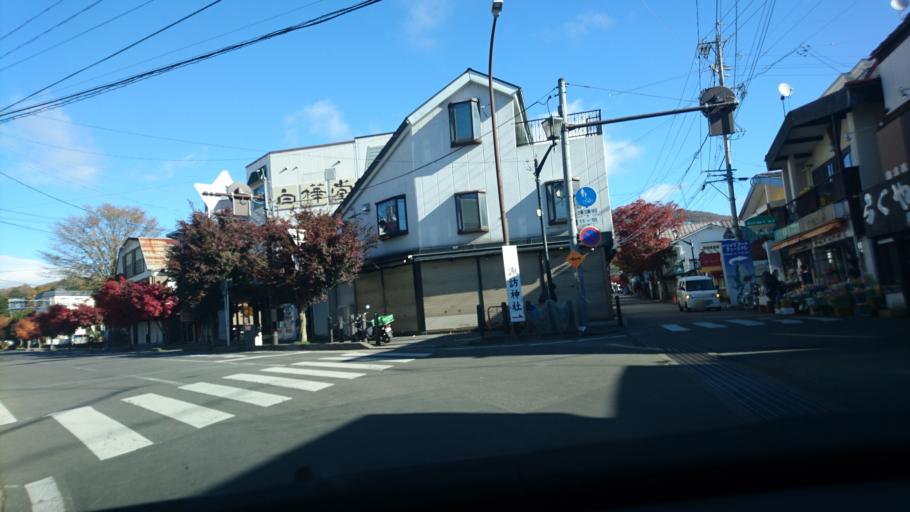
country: JP
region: Nagano
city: Komoro
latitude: 36.3572
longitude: 138.6341
